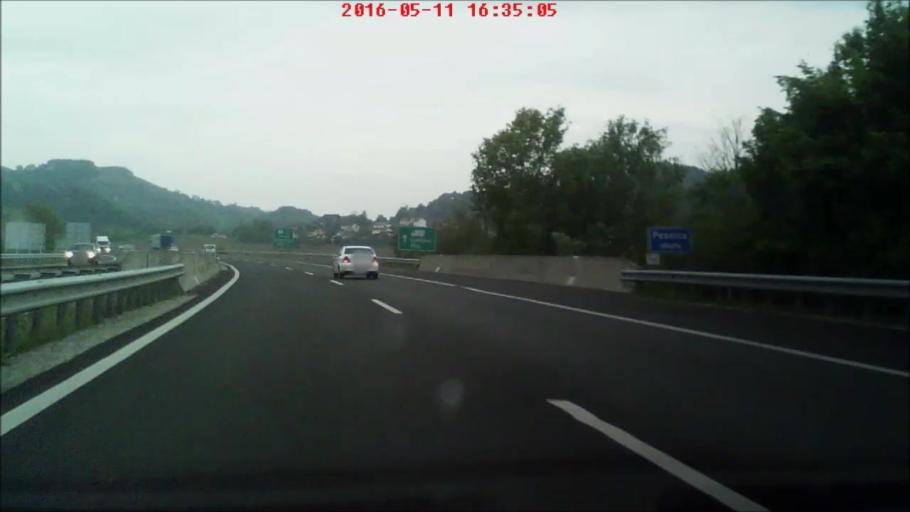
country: SI
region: Pesnica
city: Pesnica pri Mariboru
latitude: 46.6049
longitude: 15.6627
